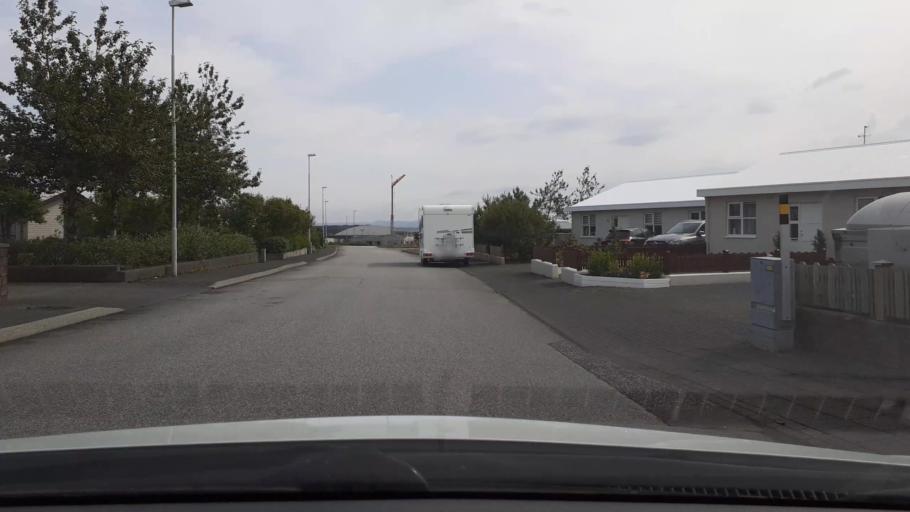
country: IS
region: Southern Peninsula
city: Reykjanesbaer
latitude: 63.9965
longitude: -22.5716
